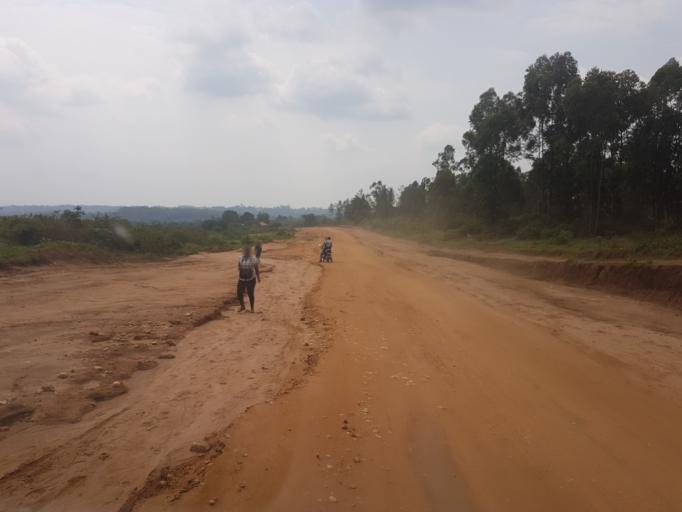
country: UG
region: Western Region
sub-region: Kanungu District
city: Ntungamo
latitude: -0.8119
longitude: 29.7062
